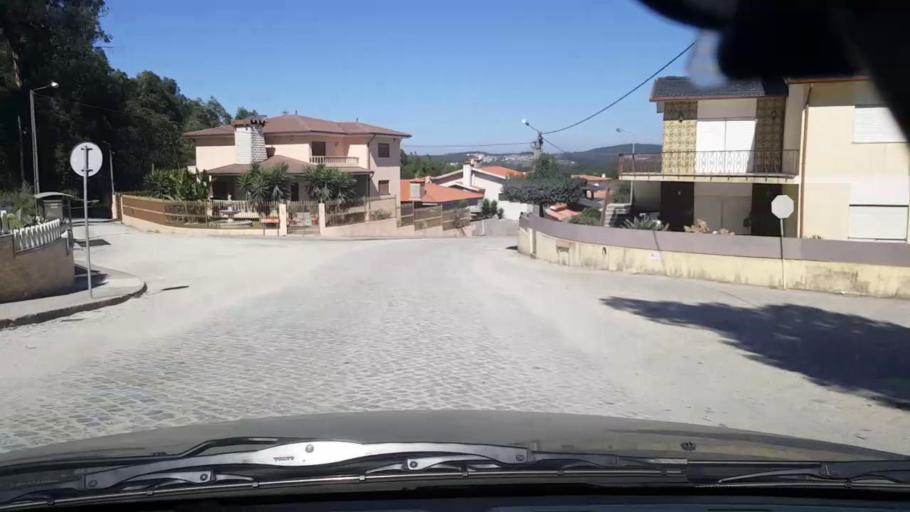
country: PT
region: Porto
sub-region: Maia
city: Gemunde
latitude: 41.3371
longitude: -8.6462
